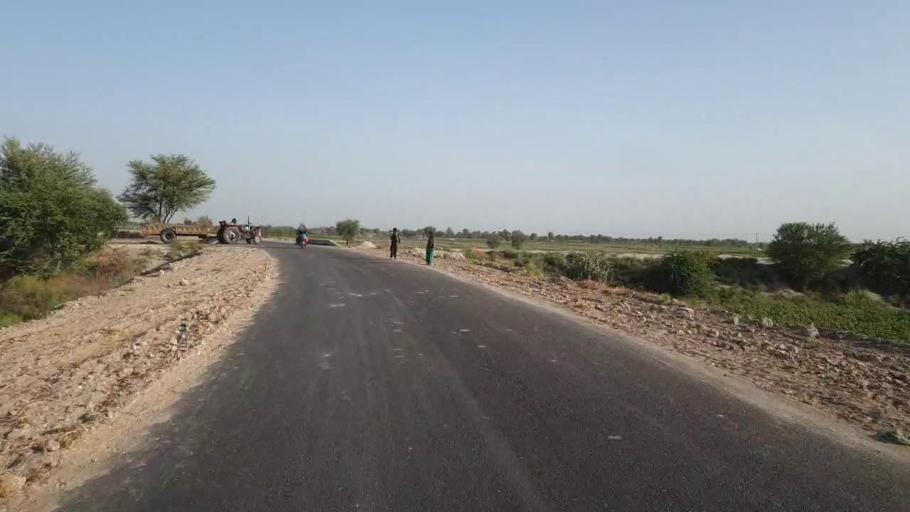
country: PK
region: Sindh
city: Jam Sahib
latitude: 26.3367
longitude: 68.5723
